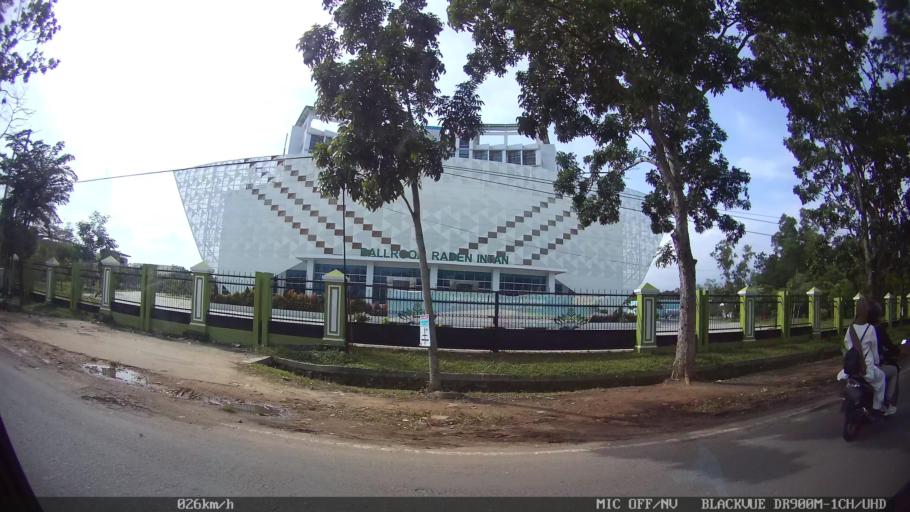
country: ID
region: Lampung
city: Kedaton
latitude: -5.3790
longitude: 105.3028
